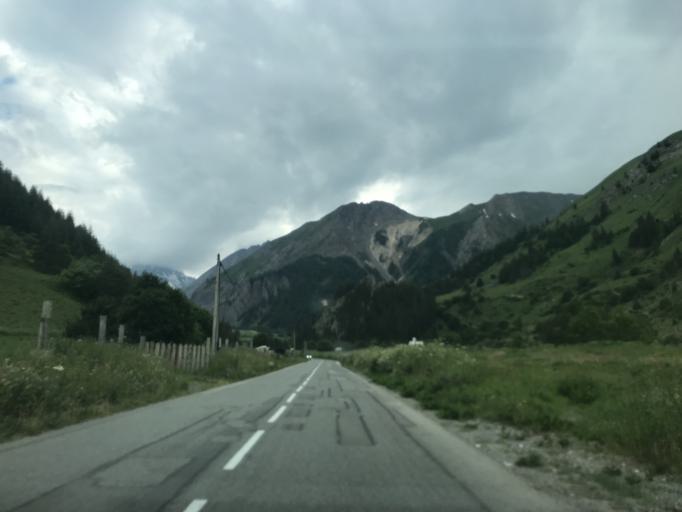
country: FR
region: Rhone-Alpes
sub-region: Departement de la Savoie
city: Valloire
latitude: 45.1324
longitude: 6.4188
